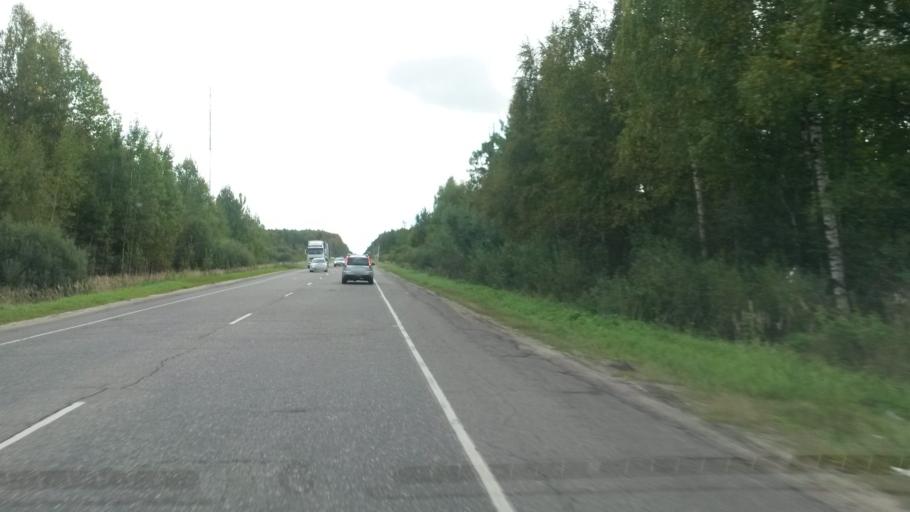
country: RU
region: Ivanovo
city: Rodniki
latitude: 57.0882
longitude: 41.6824
